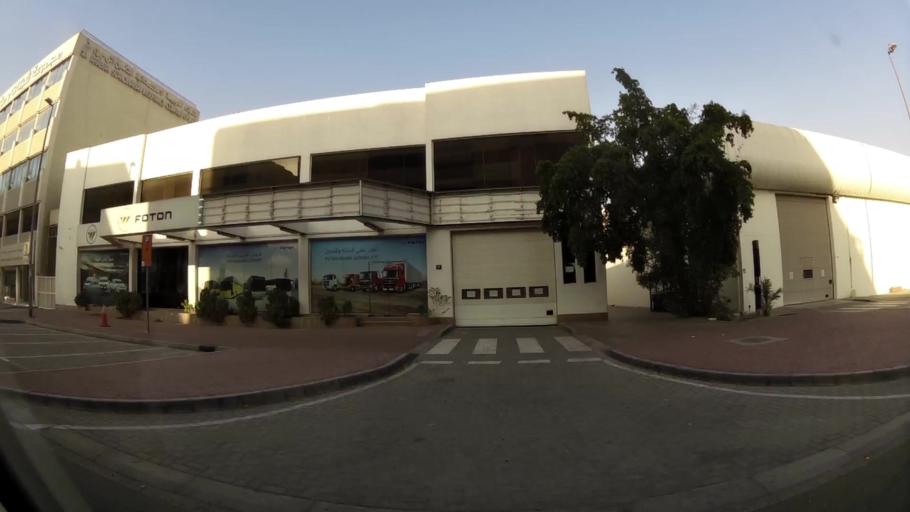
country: AE
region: Ash Shariqah
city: Sharjah
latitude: 25.2516
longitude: 55.3379
